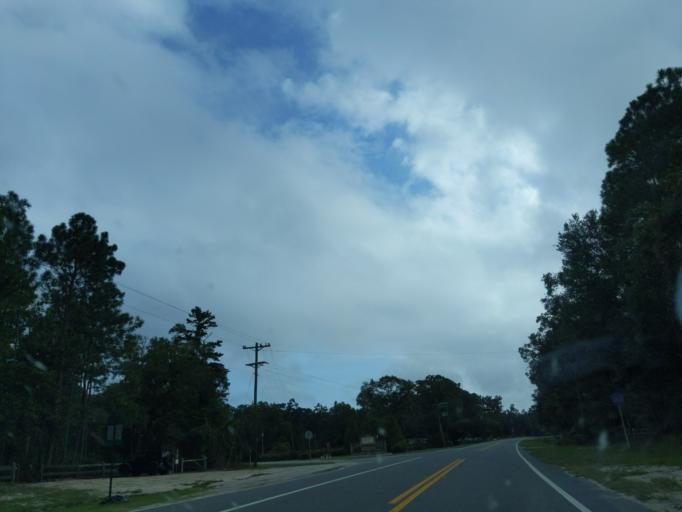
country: US
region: Florida
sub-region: Wakulla County
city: Crawfordville
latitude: 30.1216
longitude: -84.3152
